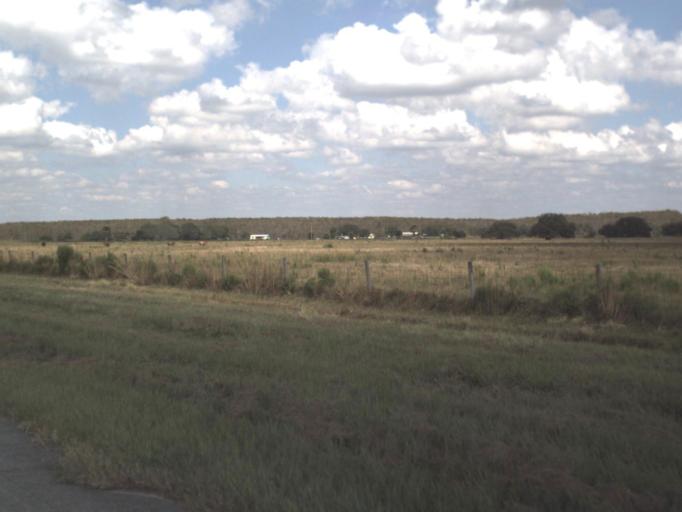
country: US
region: Florida
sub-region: Okeechobee County
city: Okeechobee
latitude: 27.3710
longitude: -80.9777
